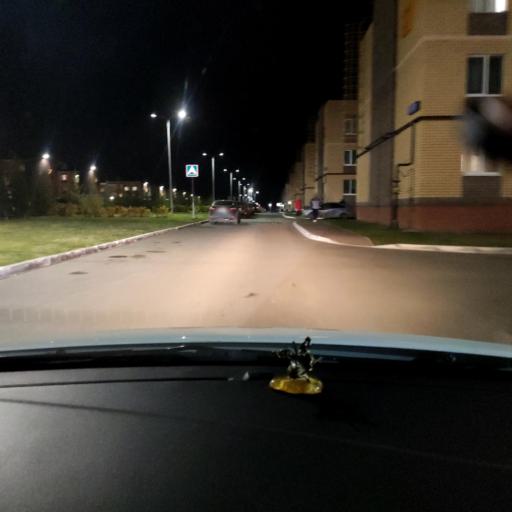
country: RU
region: Tatarstan
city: Vysokaya Gora
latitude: 55.8109
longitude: 49.4374
